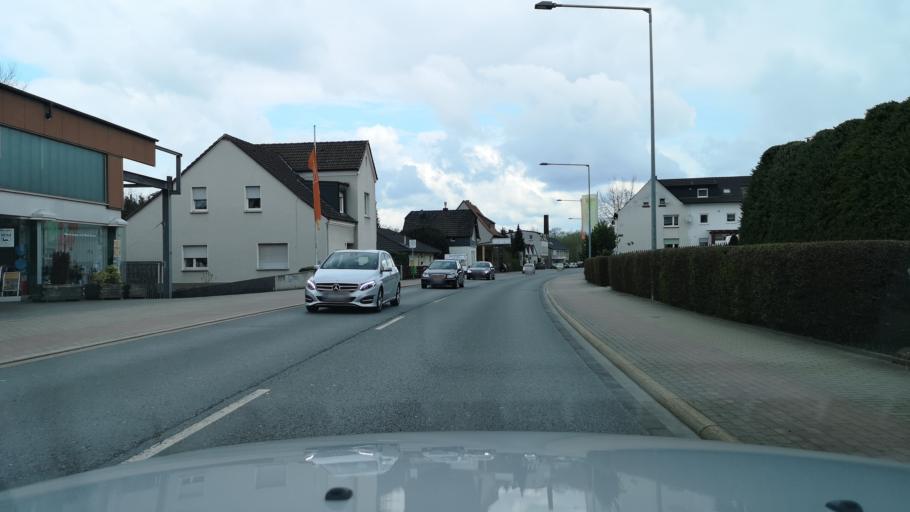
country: DE
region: North Rhine-Westphalia
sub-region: Regierungsbezirk Arnsberg
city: Menden
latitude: 51.4204
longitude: 7.8245
